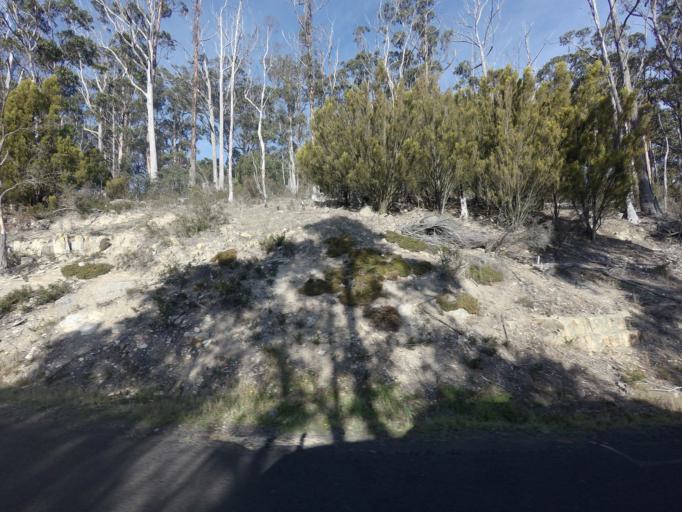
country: AU
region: Tasmania
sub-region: Sorell
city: Sorell
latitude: -42.4842
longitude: 147.4520
